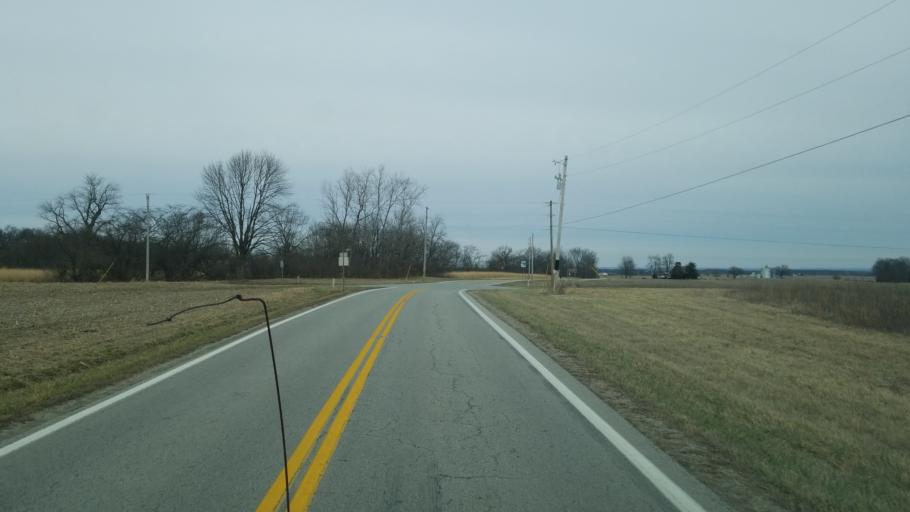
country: US
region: Ohio
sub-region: Ross County
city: Frankfort
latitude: 39.4841
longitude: -83.1823
